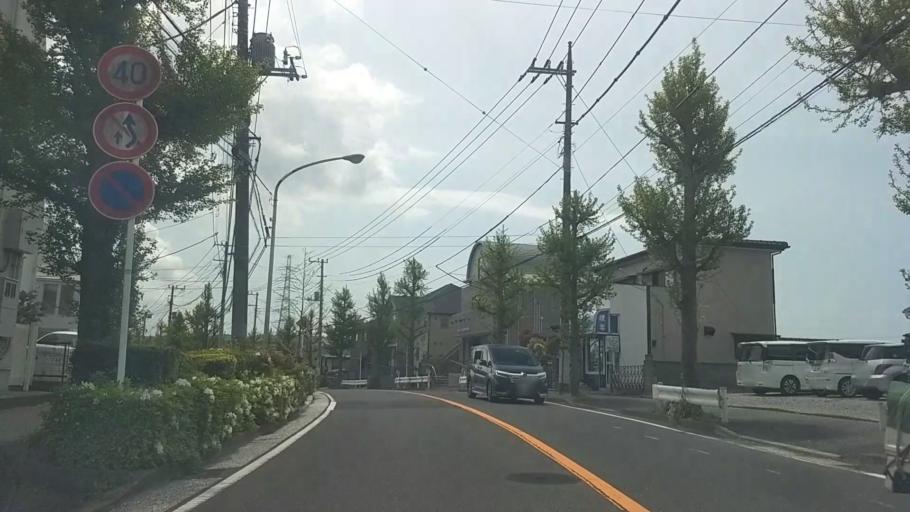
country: JP
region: Kanagawa
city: Kamakura
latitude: 35.3799
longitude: 139.5919
